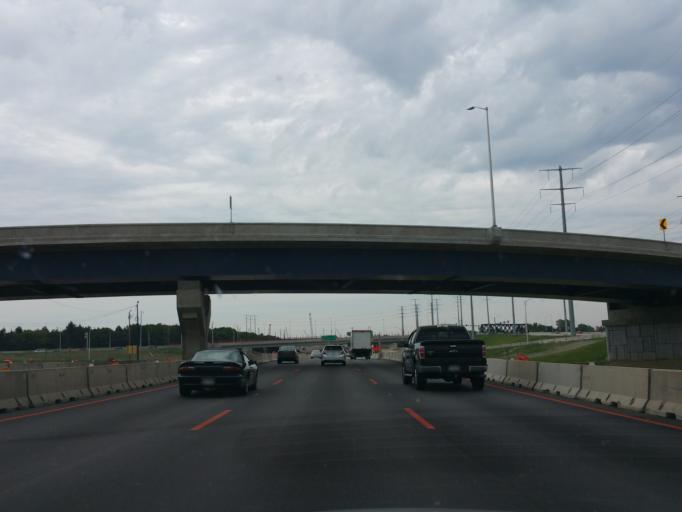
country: US
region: Wisconsin
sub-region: Waukesha County
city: Elm Grove
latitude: 43.0304
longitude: -88.0513
